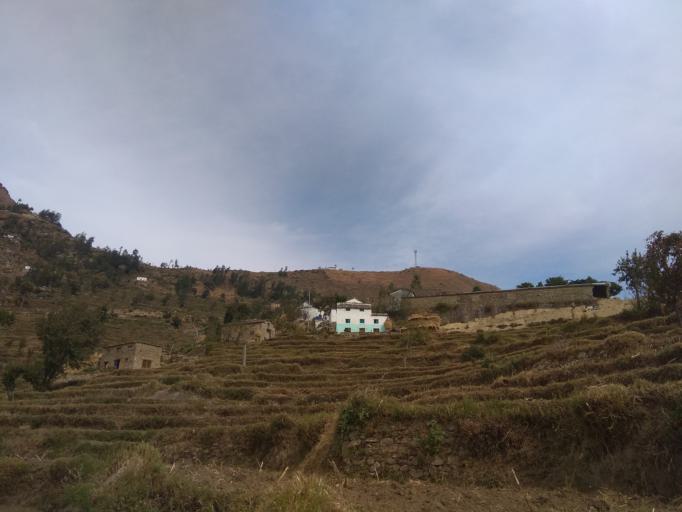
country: NP
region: Mid Western
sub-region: Bheri Zone
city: Dailekh
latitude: 29.2425
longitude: 81.6615
